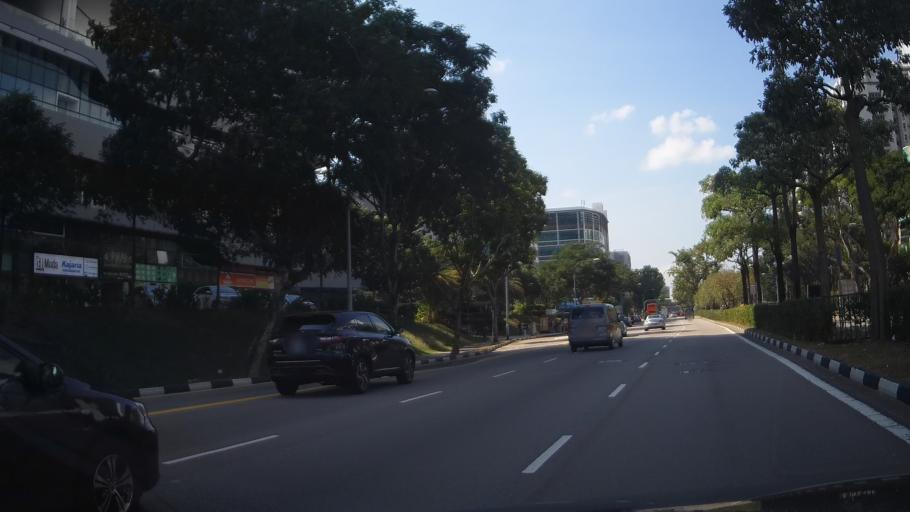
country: SG
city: Singapore
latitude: 1.3325
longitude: 103.8892
